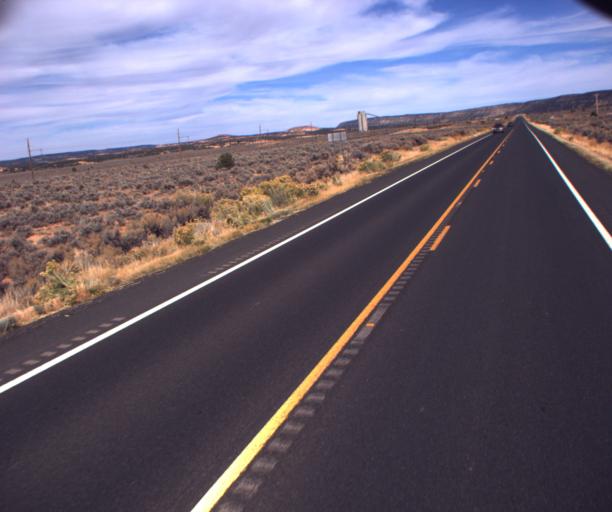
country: US
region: Arizona
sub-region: Navajo County
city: Kayenta
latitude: 36.5452
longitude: -110.5391
